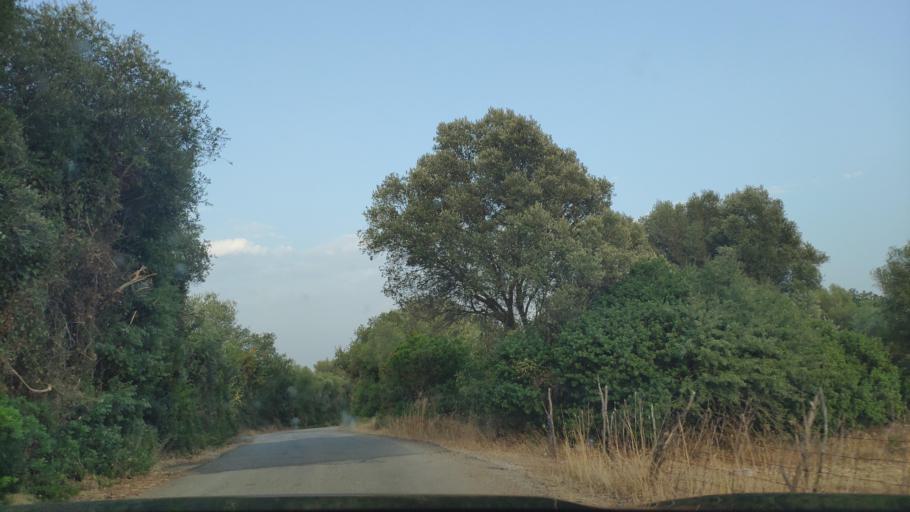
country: GR
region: West Greece
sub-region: Nomos Aitolias kai Akarnanias
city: Monastirakion
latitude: 38.9217
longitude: 20.9885
